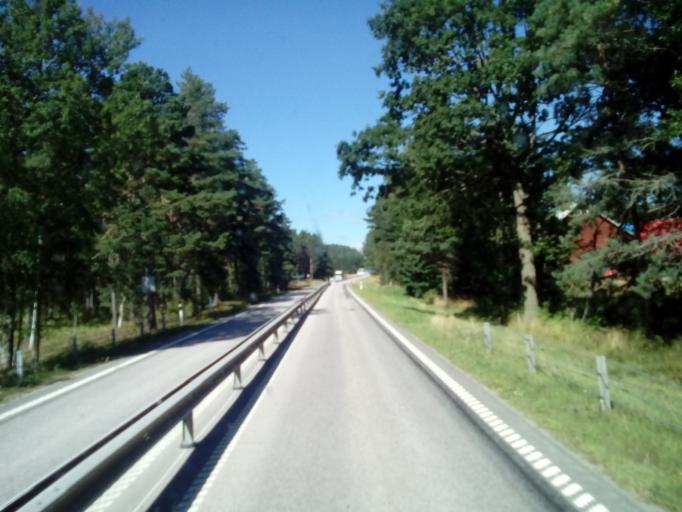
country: SE
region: OEstergoetland
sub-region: Kinda Kommun
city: Rimforsa
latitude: 58.0722
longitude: 15.6545
